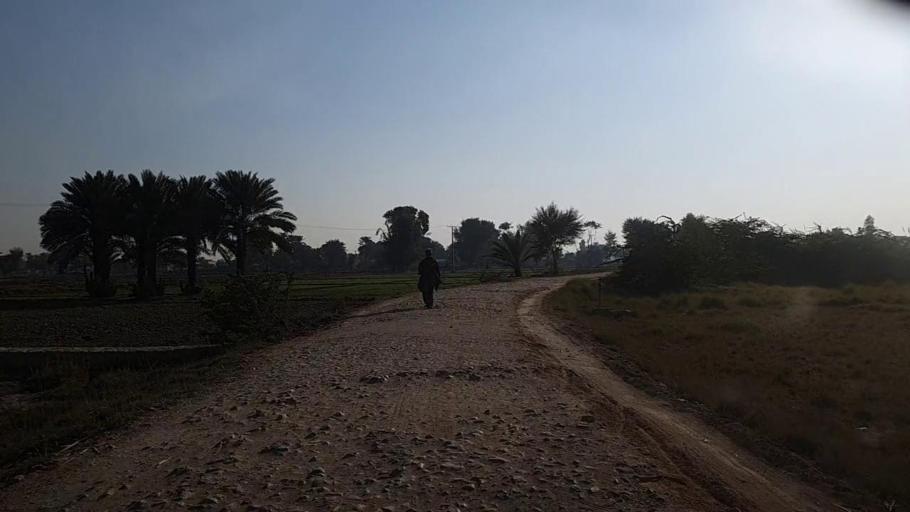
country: PK
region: Sindh
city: Ranipur
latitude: 27.2456
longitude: 68.5404
